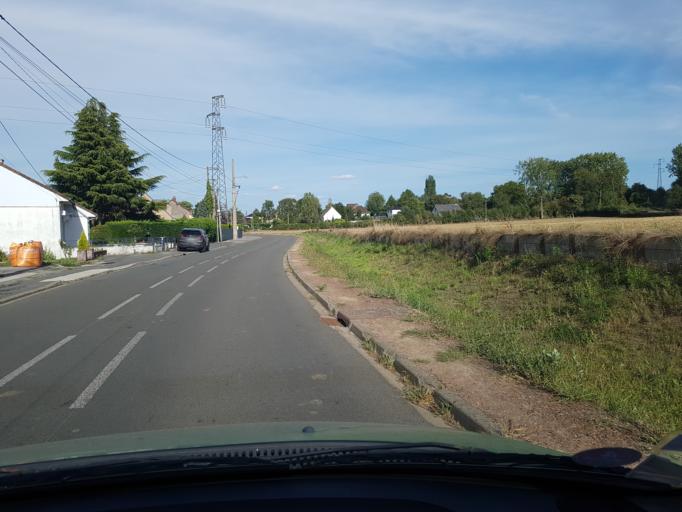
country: FR
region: Nord-Pas-de-Calais
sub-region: Departement du Pas-de-Calais
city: Labeuvriere
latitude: 50.5163
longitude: 2.5517
